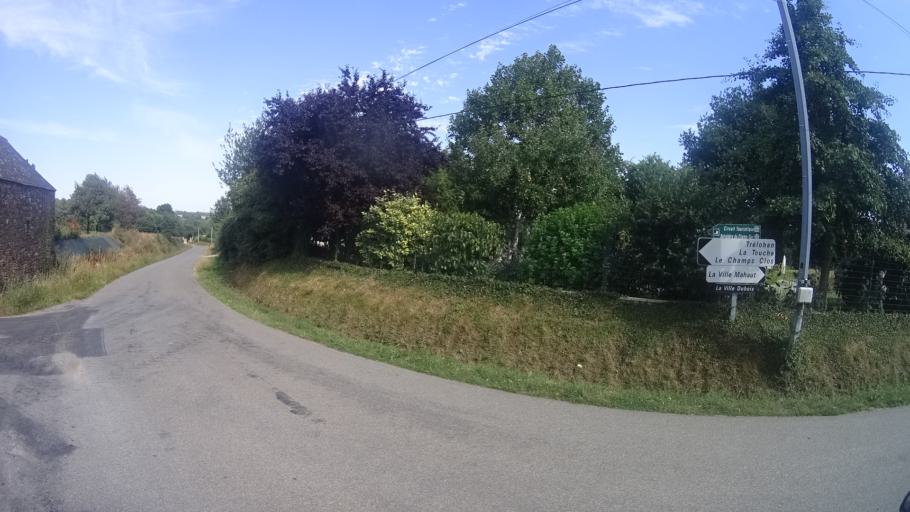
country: FR
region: Brittany
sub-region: Departement du Morbihan
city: Beganne
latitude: 47.6032
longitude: -2.2047
